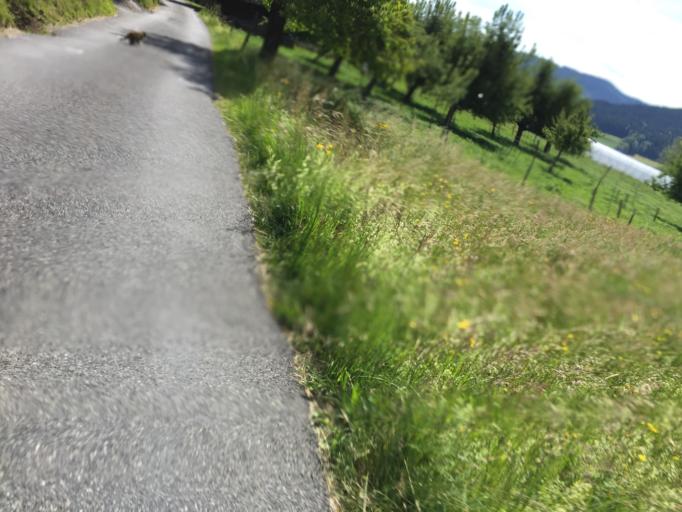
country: CH
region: Bern
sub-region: Bern-Mittelland District
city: Taegertschi
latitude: 46.8809
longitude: 7.5887
